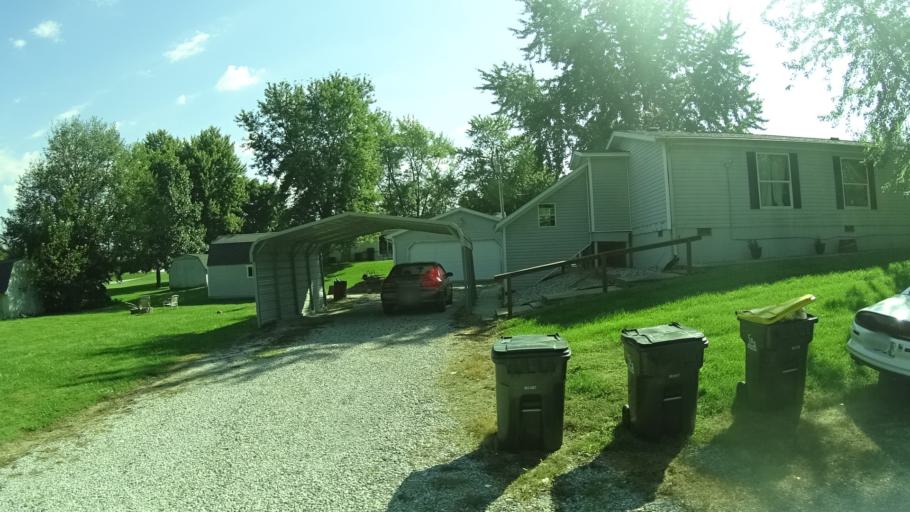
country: US
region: Indiana
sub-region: Madison County
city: Lapel
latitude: 40.0750
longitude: -85.8498
